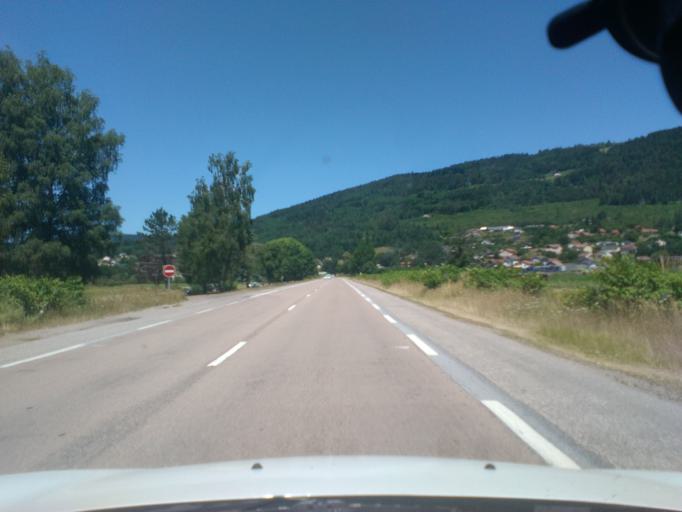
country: FR
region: Lorraine
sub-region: Departement des Vosges
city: Vagney
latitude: 48.0187
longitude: 6.7067
